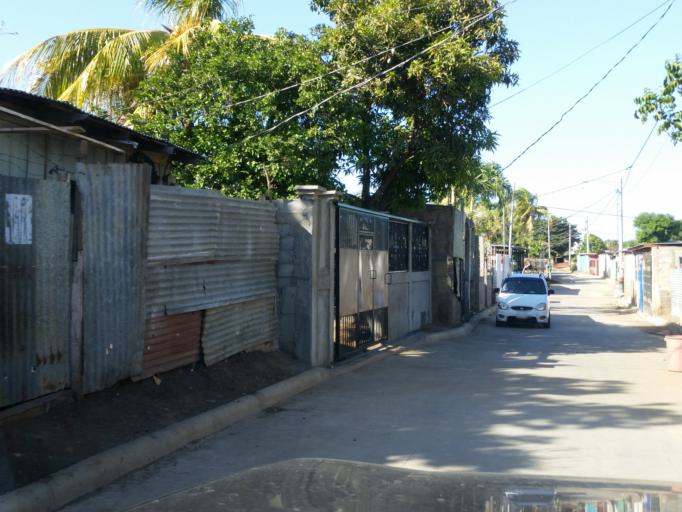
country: NI
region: Managua
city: Managua
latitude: 12.1287
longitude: -86.2790
